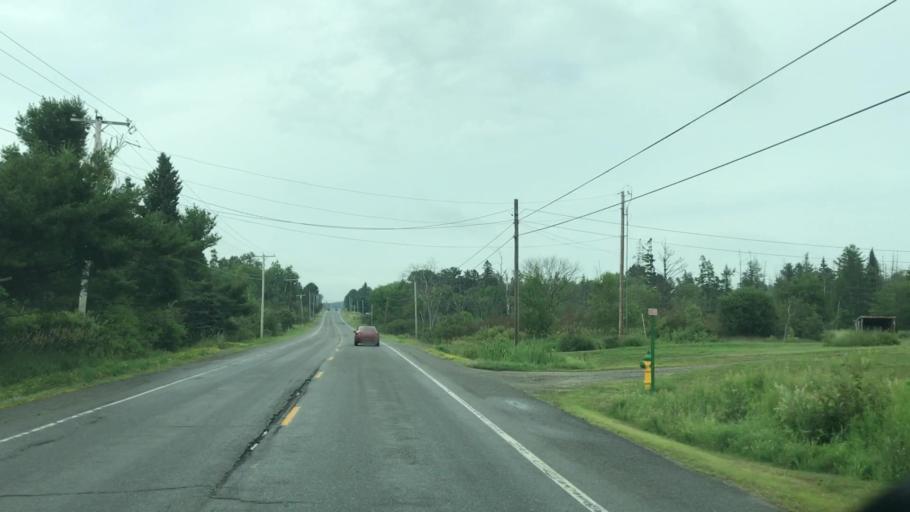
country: US
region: Maine
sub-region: Penobscot County
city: Lincoln
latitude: 45.3474
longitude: -68.5497
